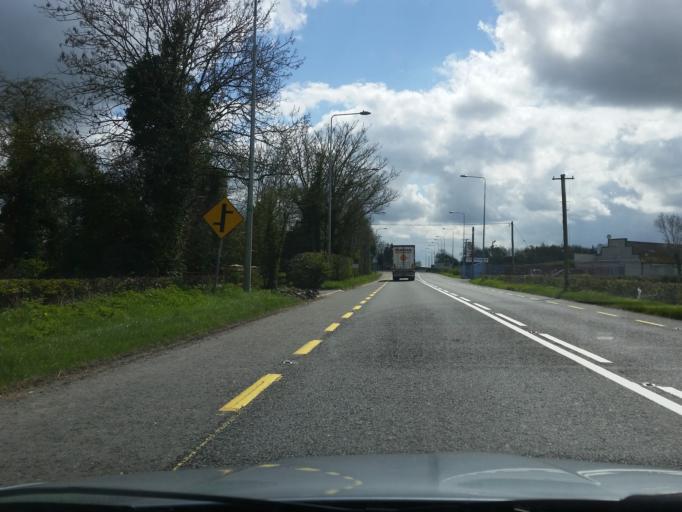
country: IE
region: Leinster
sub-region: An Mhi
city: Ratoath
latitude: 53.5744
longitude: -6.4510
